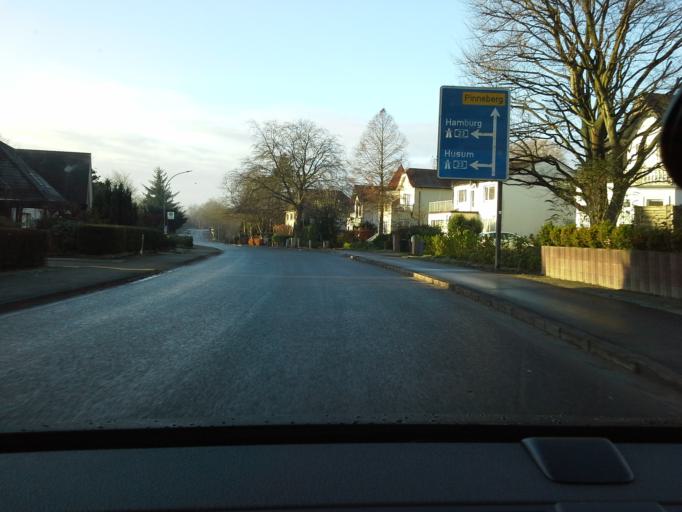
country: DE
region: Schleswig-Holstein
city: Borstel-Hohenraden
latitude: 53.6809
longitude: 9.8015
